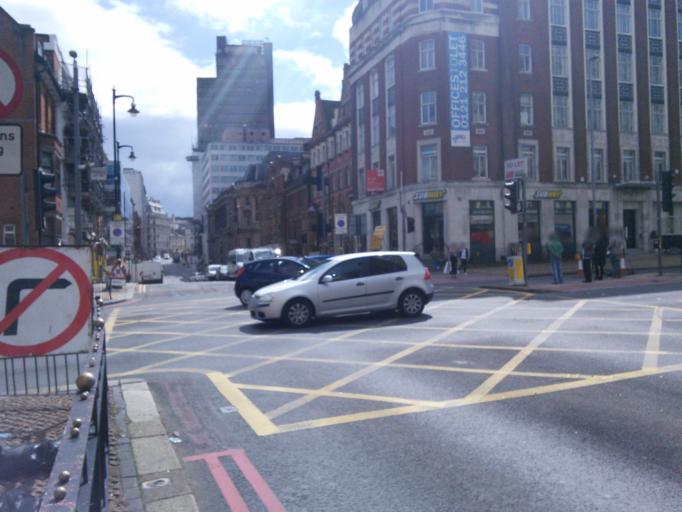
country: GB
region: England
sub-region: City and Borough of Birmingham
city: Birmingham
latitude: 52.4825
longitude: -1.9035
